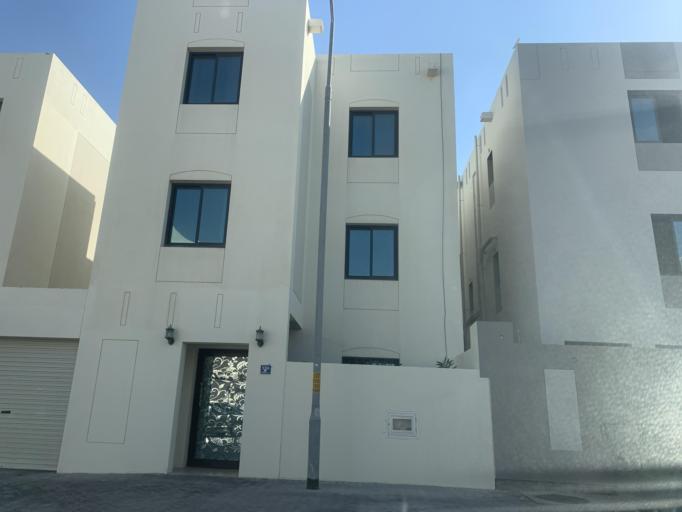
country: BH
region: Central Governorate
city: Madinat Hamad
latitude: 26.1246
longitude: 50.4840
